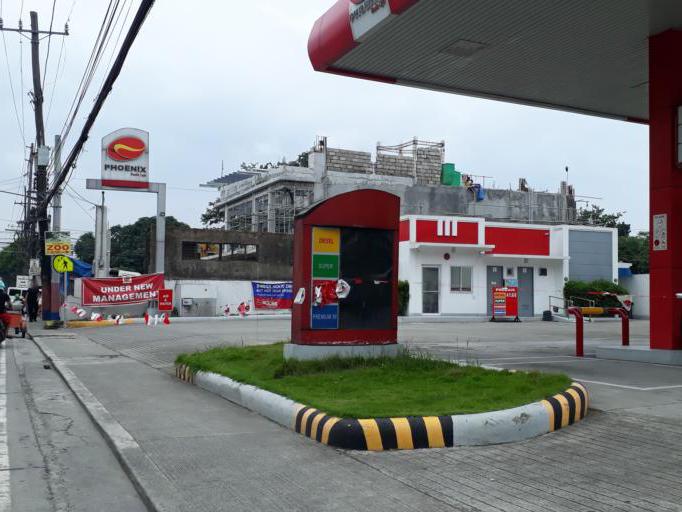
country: PH
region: Metro Manila
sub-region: Caloocan City
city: Niugan
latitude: 14.6642
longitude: 120.9841
